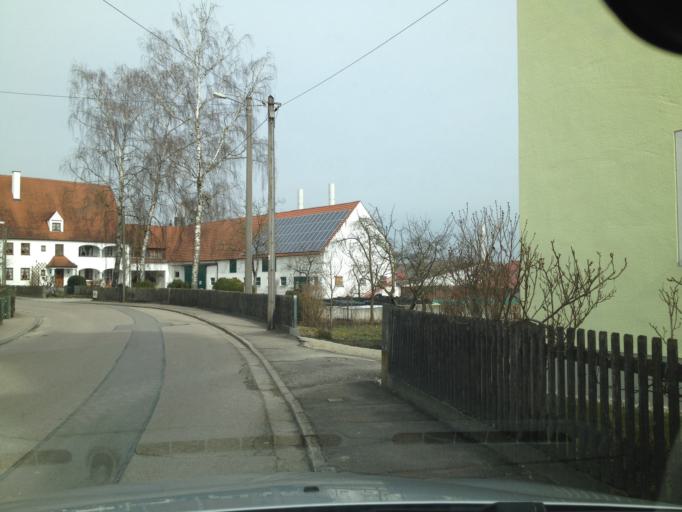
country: DE
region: Bavaria
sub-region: Swabia
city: Buttenwiesen
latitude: 48.5989
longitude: 10.7068
